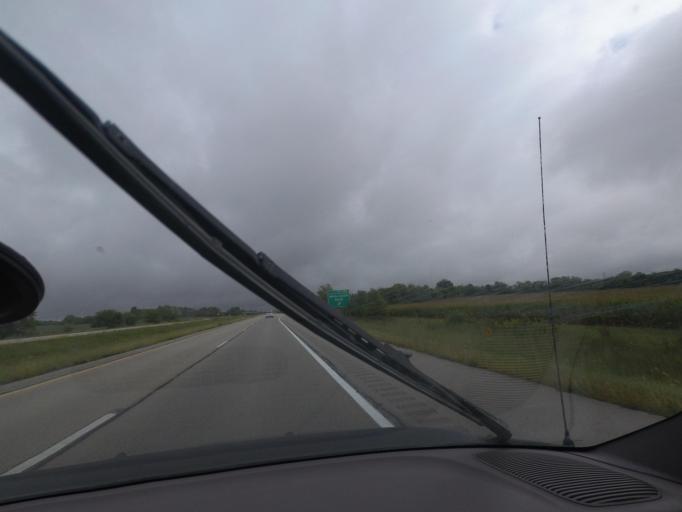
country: US
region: Illinois
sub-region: Piatt County
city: Monticello
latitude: 40.0786
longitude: -88.5300
